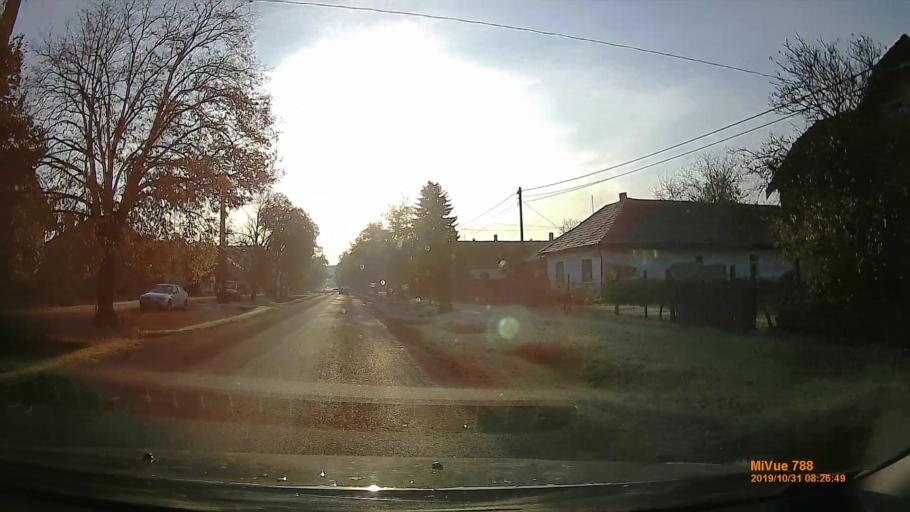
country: HU
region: Pest
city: Tapiobicske
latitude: 47.3642
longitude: 19.6816
